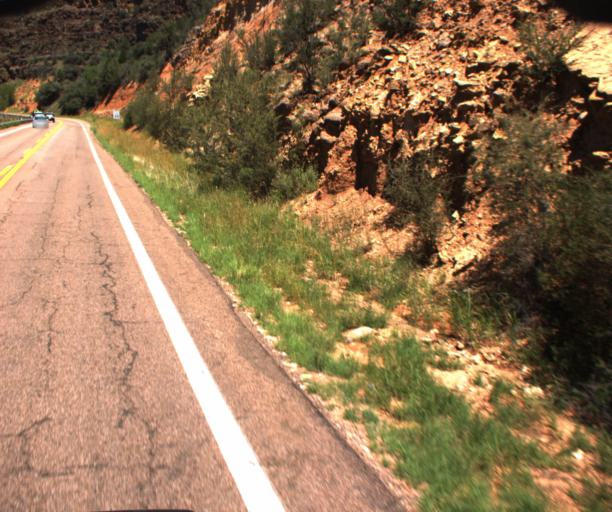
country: US
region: Arizona
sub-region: Navajo County
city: Cibecue
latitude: 34.0328
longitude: -110.2376
